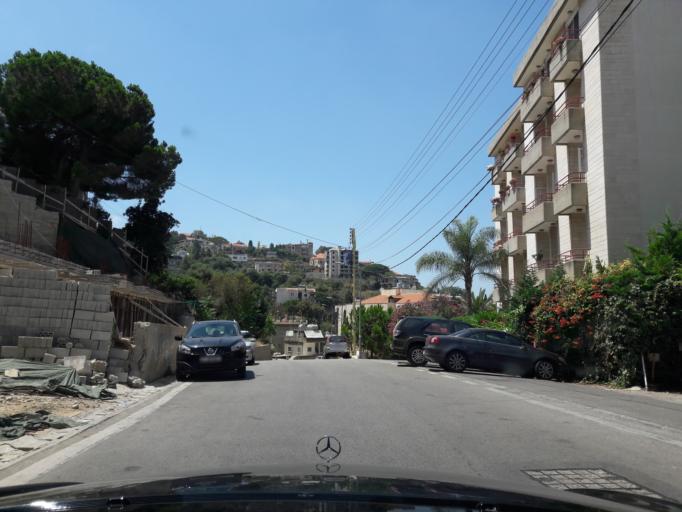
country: LB
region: Mont-Liban
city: Djounie
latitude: 33.9209
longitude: 35.6407
